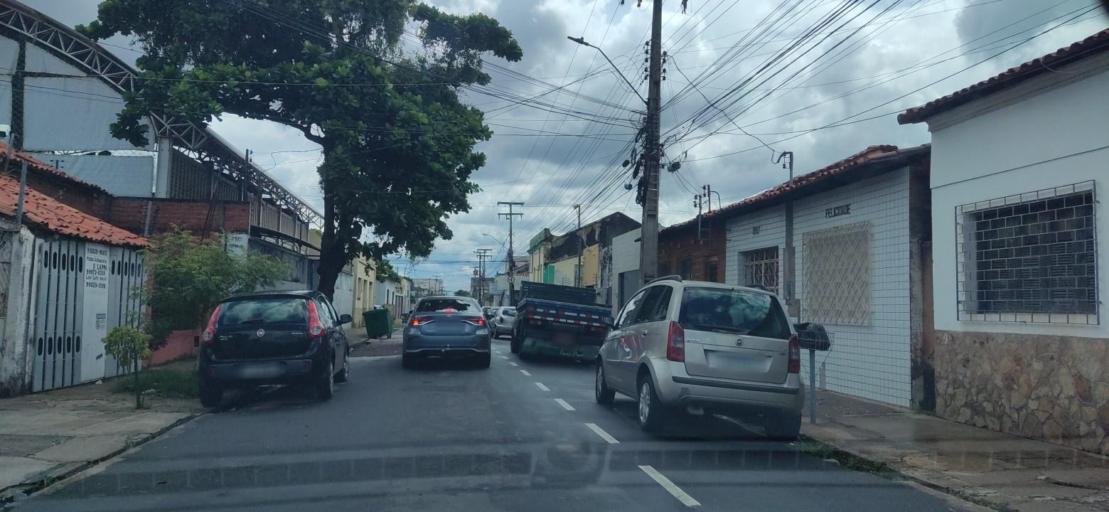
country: BR
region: Piaui
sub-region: Teresina
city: Teresina
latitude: -5.0851
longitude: -42.8101
